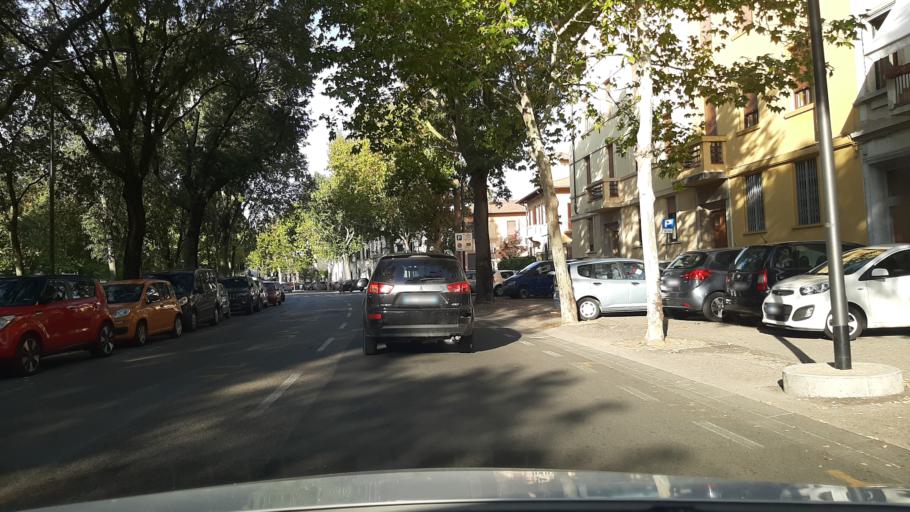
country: IT
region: Tuscany
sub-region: Province of Florence
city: Fiesole
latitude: 43.7821
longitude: 11.2854
